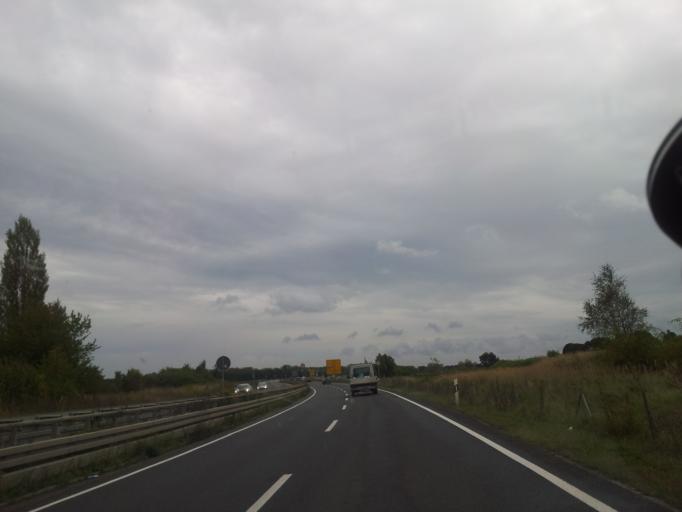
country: DE
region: Saxony-Anhalt
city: Egeln
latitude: 51.9591
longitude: 11.4460
